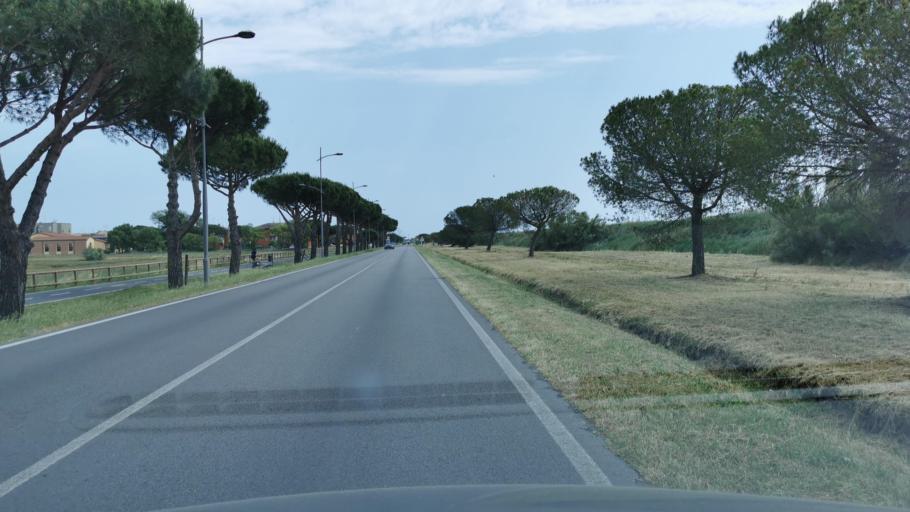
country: IT
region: Emilia-Romagna
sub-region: Provincia di Ferrara
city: Comacchio
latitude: 44.6884
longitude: 12.1902
